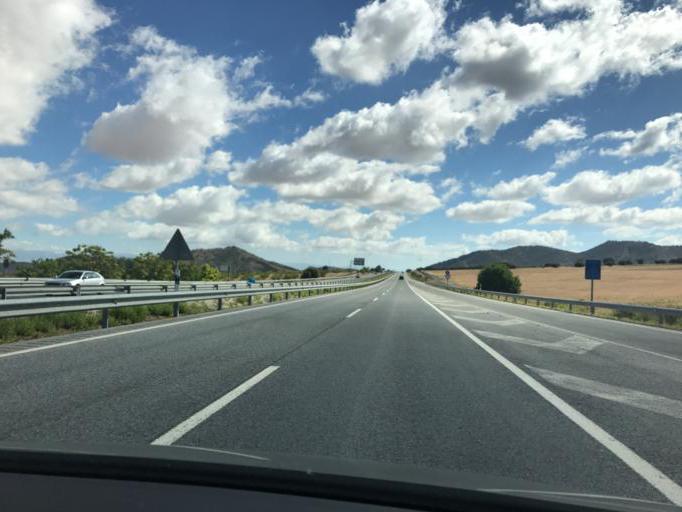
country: ES
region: Andalusia
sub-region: Provincia de Granada
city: Freila
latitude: 37.4467
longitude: -2.8887
